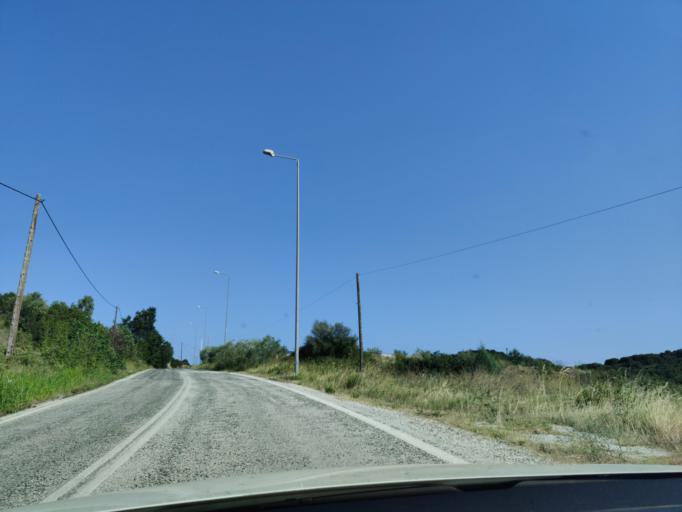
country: GR
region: East Macedonia and Thrace
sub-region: Nomos Kavalas
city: Nea Iraklitsa
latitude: 40.8606
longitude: 24.3026
